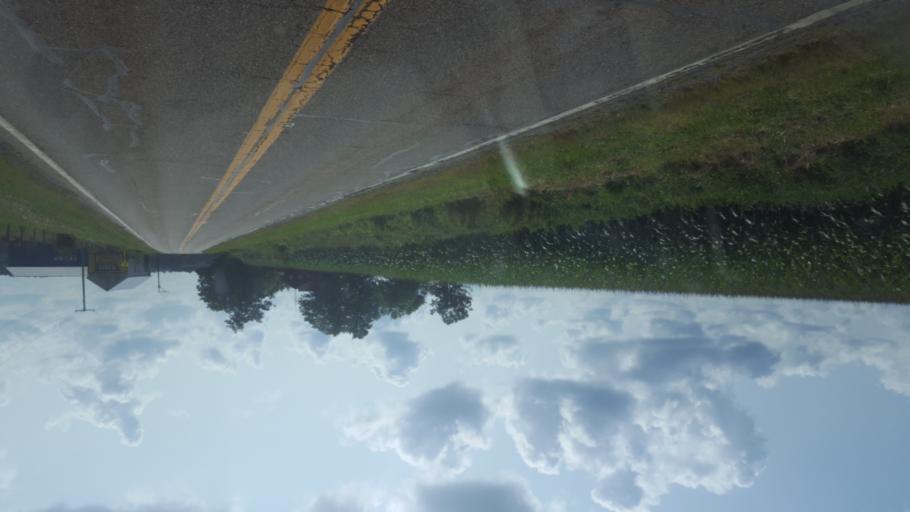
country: US
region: Ohio
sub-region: Stark County
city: Minerva
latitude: 40.7997
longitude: -81.0784
